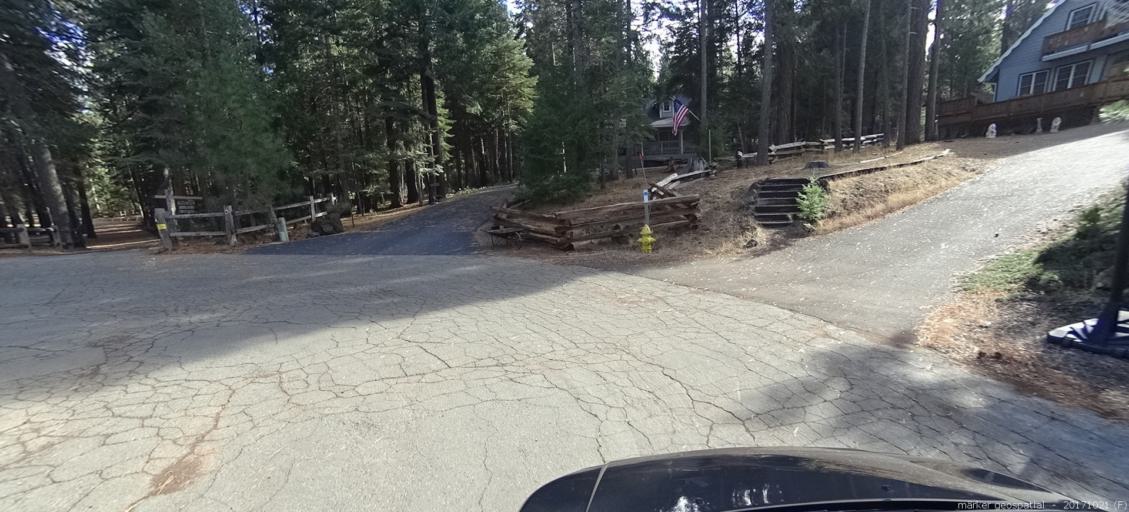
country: US
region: California
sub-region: Shasta County
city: Burney
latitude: 40.8707
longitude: -121.6695
